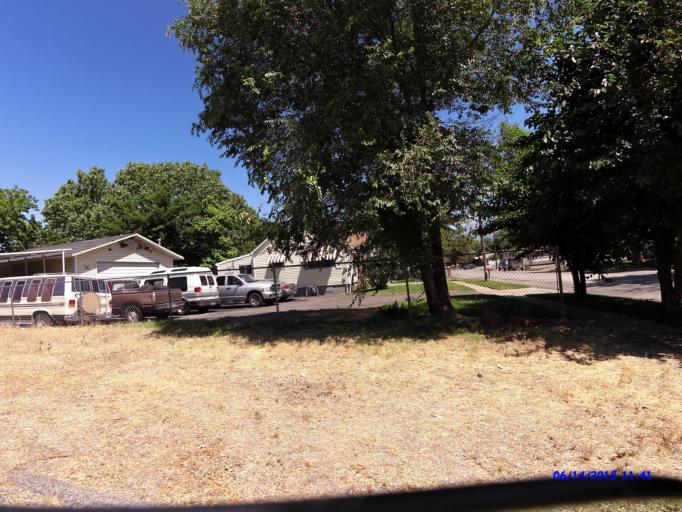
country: US
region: Utah
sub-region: Weber County
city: Ogden
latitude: 41.2221
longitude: -111.9974
